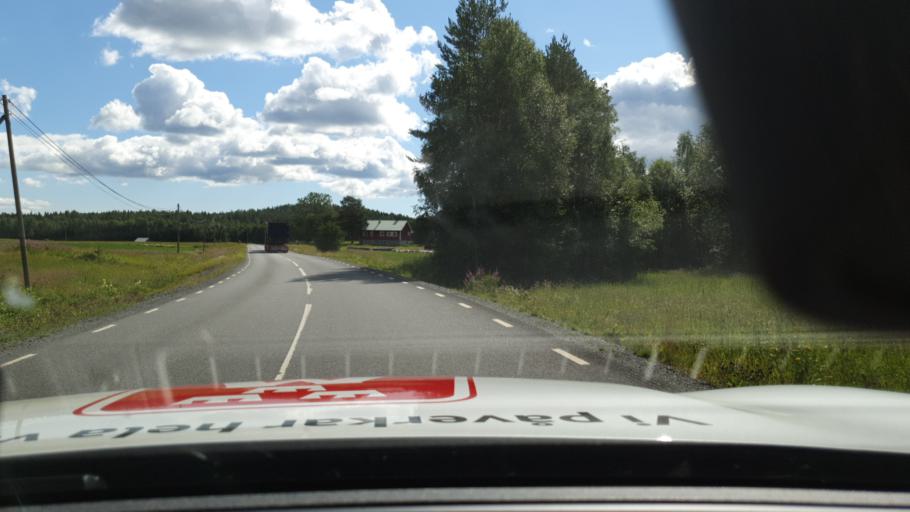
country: SE
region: Norrbotten
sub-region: Lulea Kommun
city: Sodra Sunderbyn
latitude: 65.8243
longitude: 21.9817
